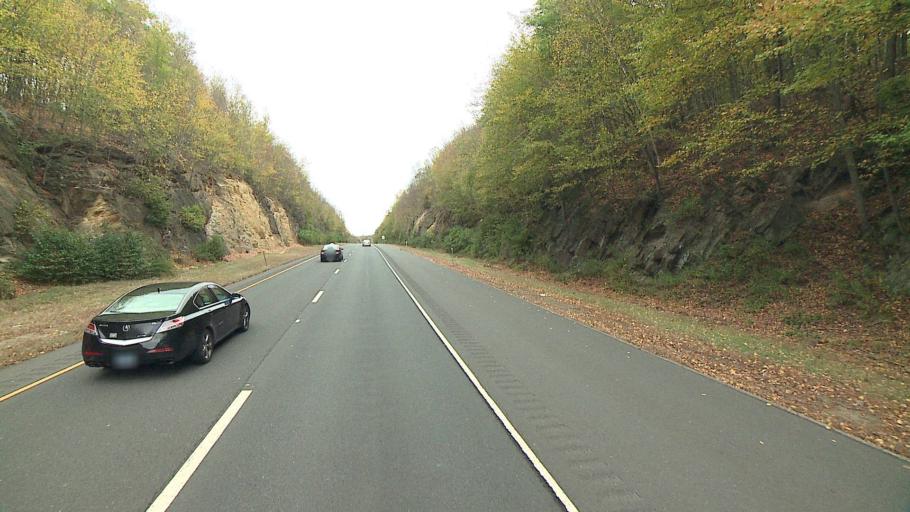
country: US
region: Connecticut
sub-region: Middlesex County
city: East Haddam
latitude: 41.4465
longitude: -72.5212
